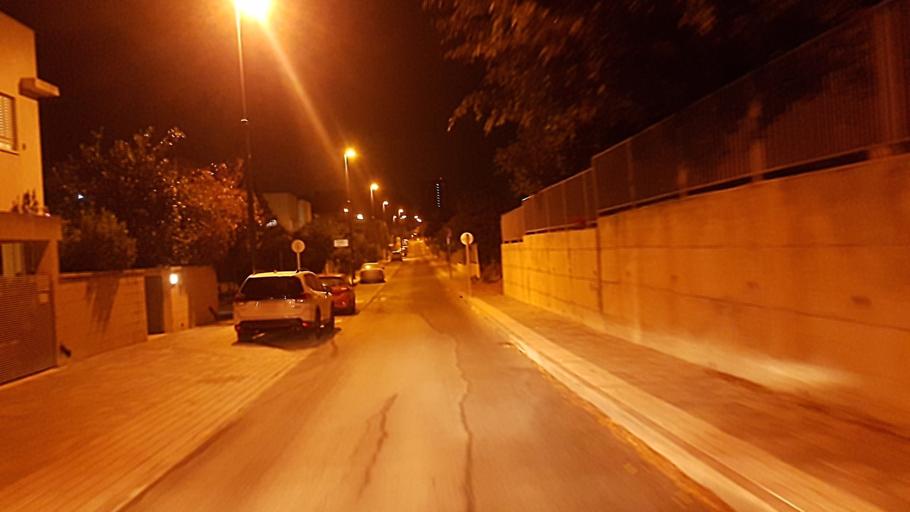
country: IL
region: Central District
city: Hod HaSharon
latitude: 32.1645
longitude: 34.8914
